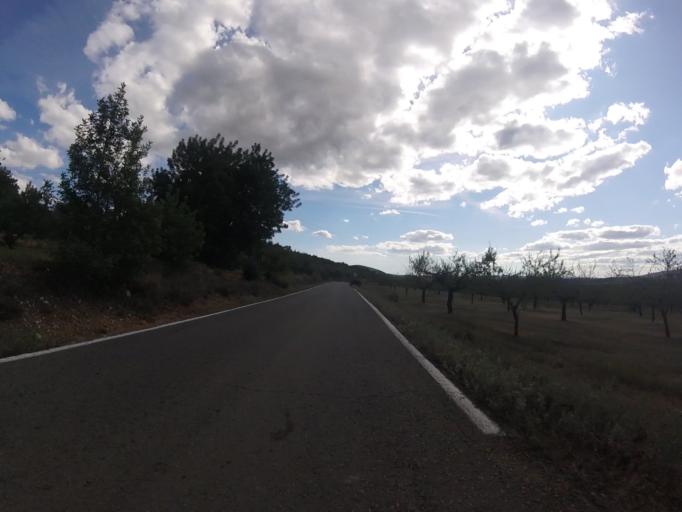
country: ES
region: Valencia
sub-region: Provincia de Castello
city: Cuevas de Vinroma
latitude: 40.3606
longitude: 0.1247
